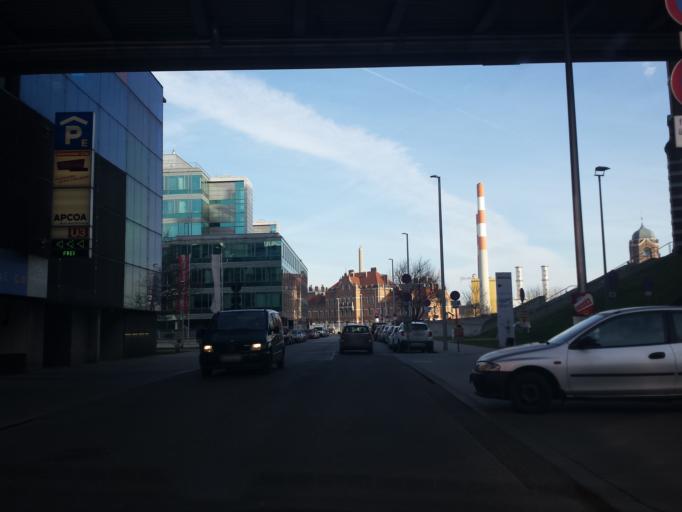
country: AT
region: Vienna
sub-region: Wien Stadt
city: Vienna
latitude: 48.1853
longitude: 16.4210
